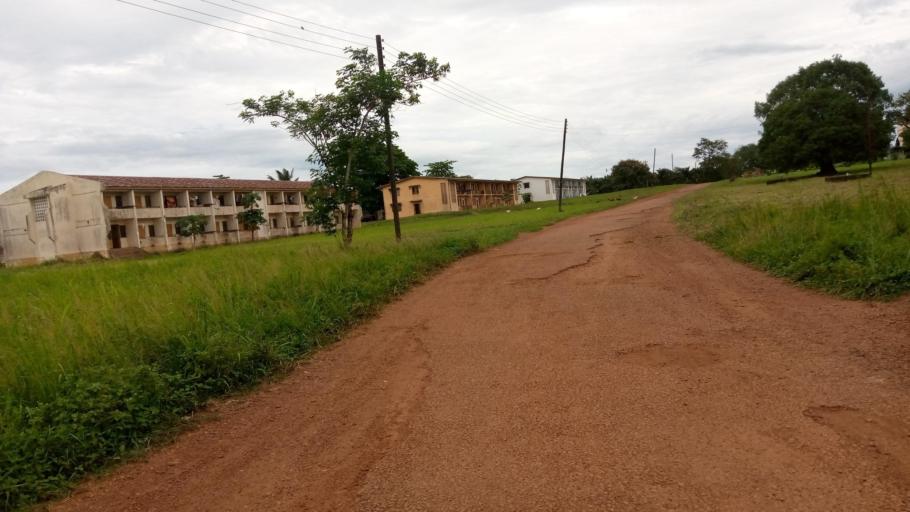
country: SL
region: Southern Province
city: Largo
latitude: 8.1178
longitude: -12.0713
